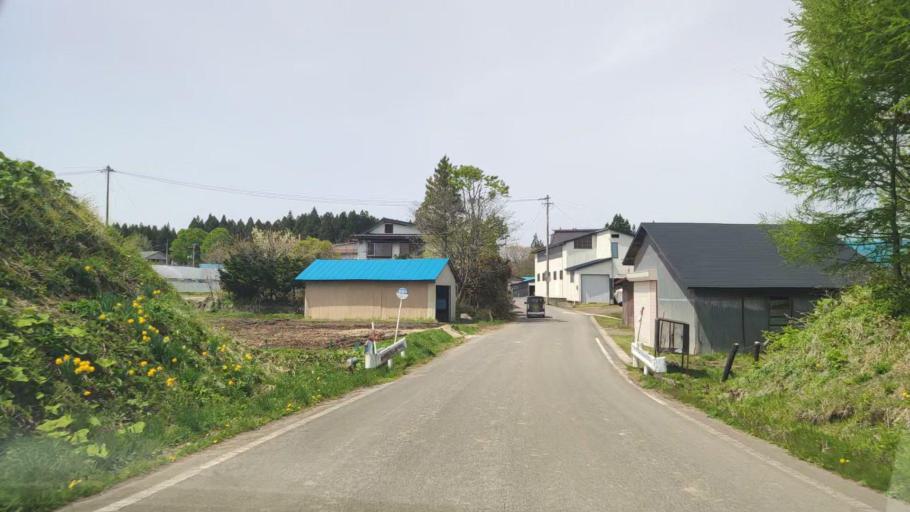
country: JP
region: Aomori
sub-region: Misawa Shi
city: Inuotose
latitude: 40.7790
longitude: 141.1226
